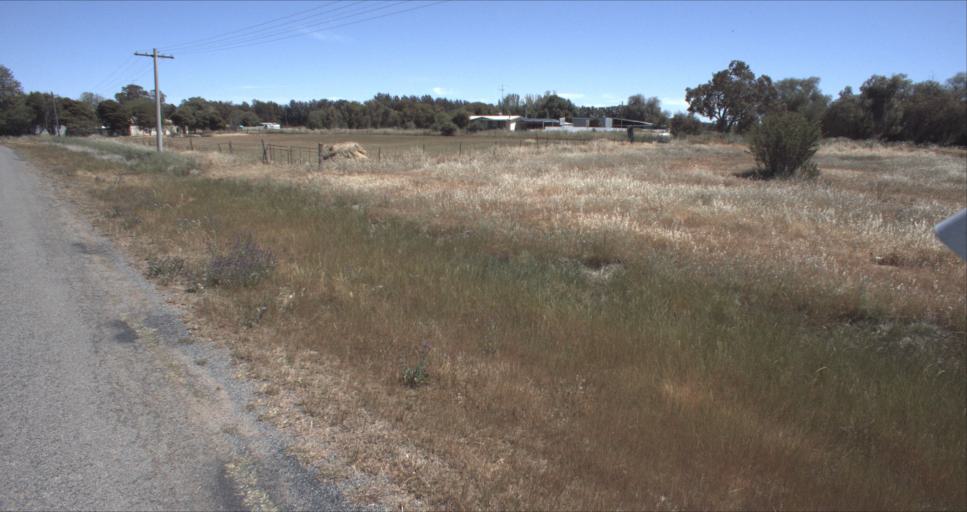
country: AU
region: New South Wales
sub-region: Leeton
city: Leeton
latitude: -34.5264
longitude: 146.3323
